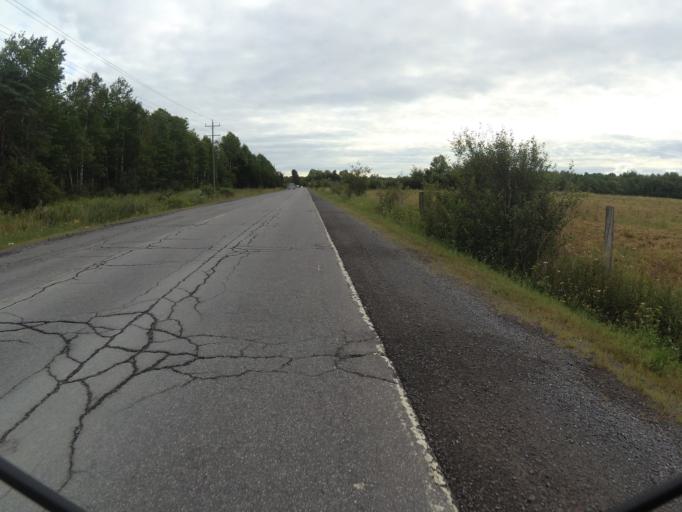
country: CA
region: Ontario
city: Bourget
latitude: 45.3509
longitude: -75.2863
